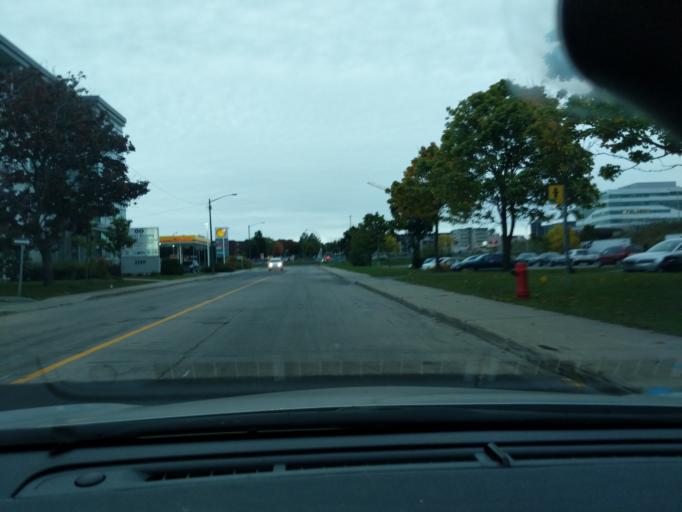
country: CA
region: Quebec
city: L'Ancienne-Lorette
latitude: 46.7649
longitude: -71.3160
